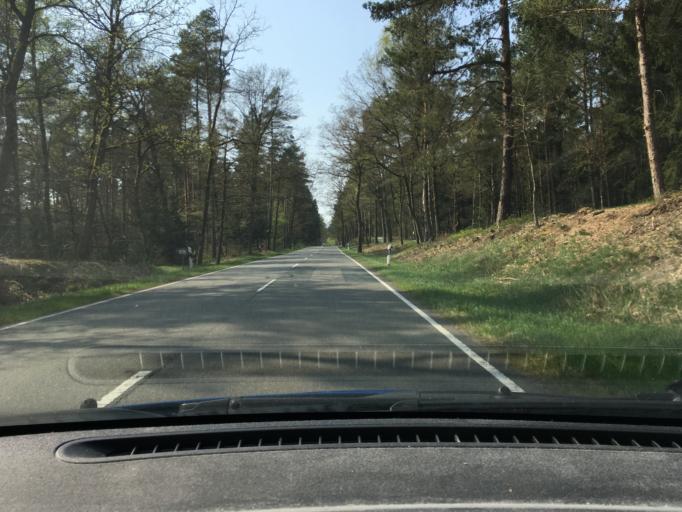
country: DE
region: Lower Saxony
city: Unterluss
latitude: 52.8662
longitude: 10.2562
